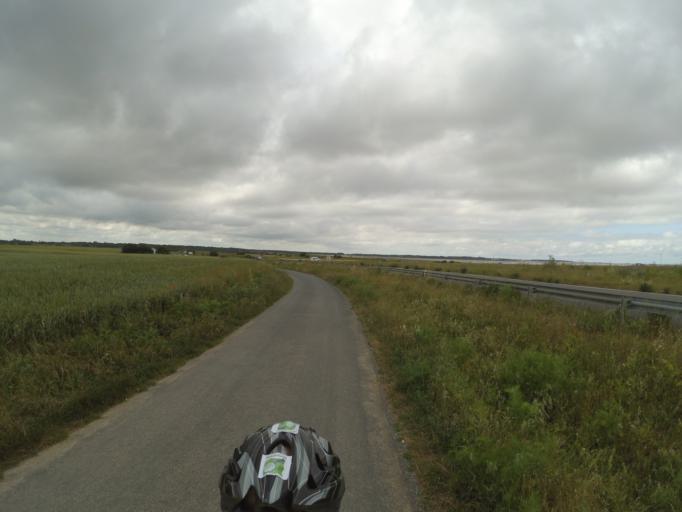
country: FR
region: Poitou-Charentes
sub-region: Departement de la Charente-Maritime
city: Yves
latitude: 46.0143
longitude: -1.0492
